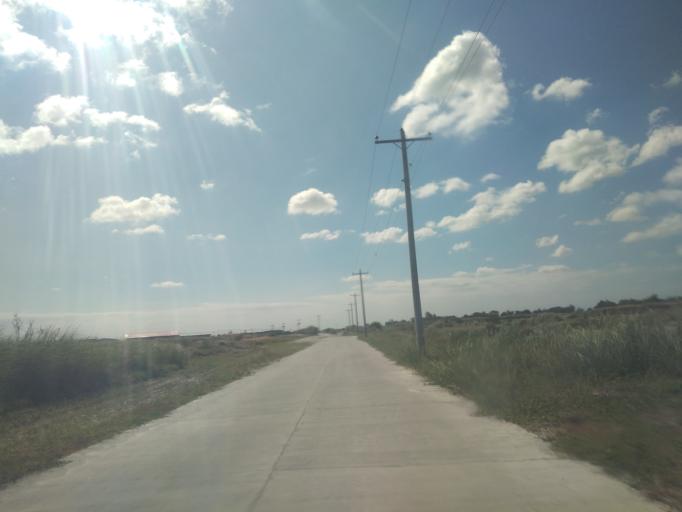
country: PH
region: Central Luzon
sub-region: Province of Pampanga
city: Balas
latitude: 15.0686
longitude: 120.5909
